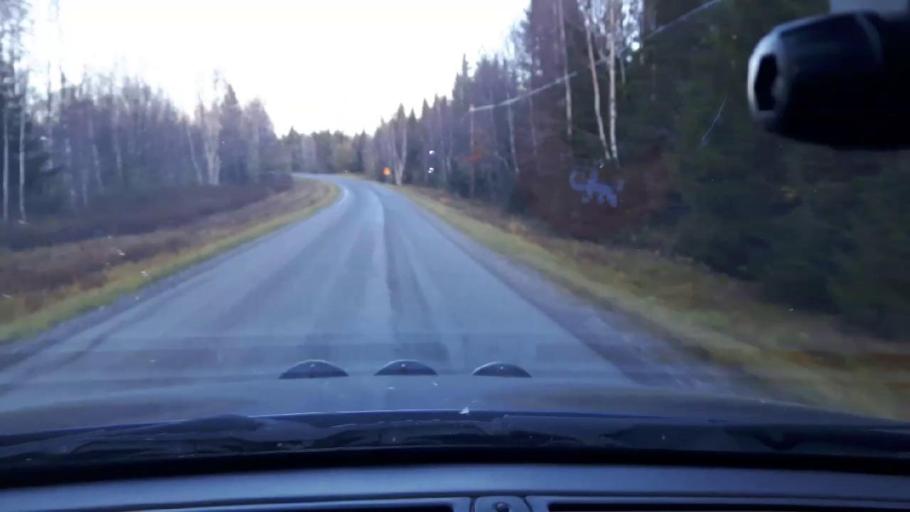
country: SE
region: Jaemtland
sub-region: Bergs Kommun
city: Hoverberg
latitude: 63.0664
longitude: 14.2640
